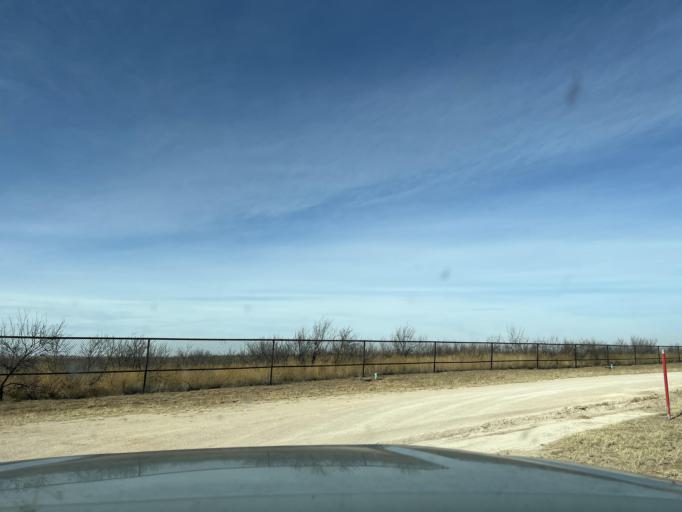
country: US
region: Texas
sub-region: Andrews County
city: Andrews
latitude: 32.4523
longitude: -102.5713
